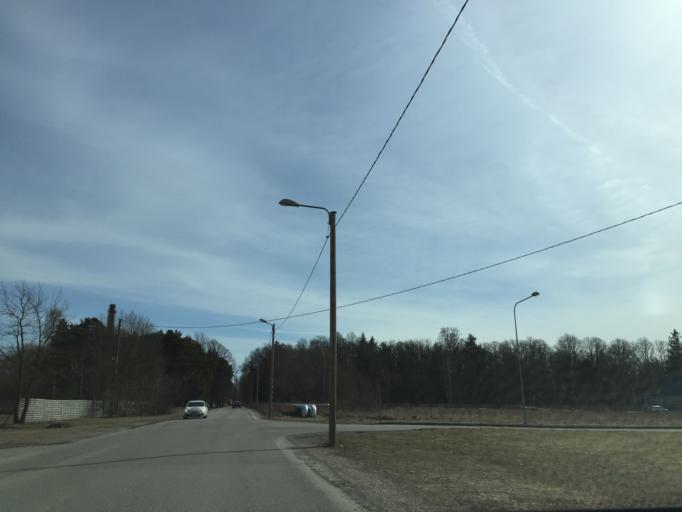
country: EE
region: Paernumaa
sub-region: Paernu linn
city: Parnu
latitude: 58.3799
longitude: 24.5331
